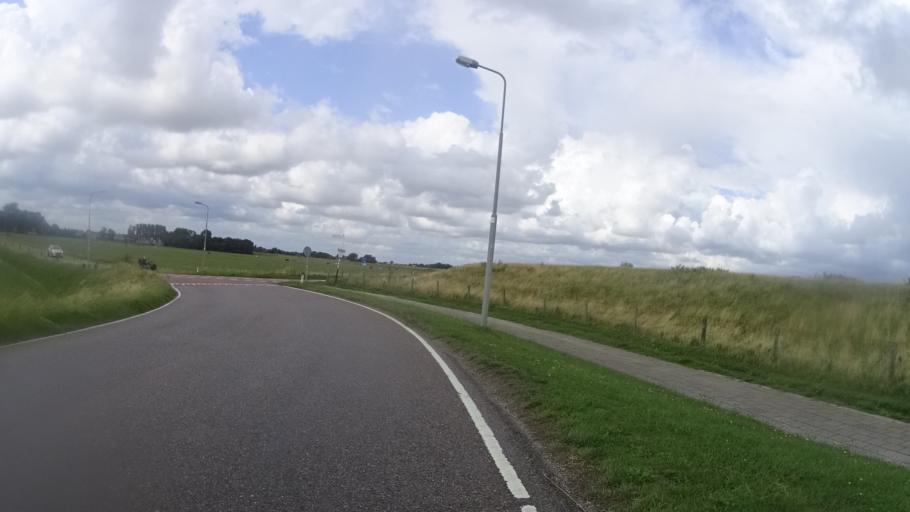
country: NL
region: North Holland
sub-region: Gemeente Schagen
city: Schagen
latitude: 52.7968
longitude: 4.7739
